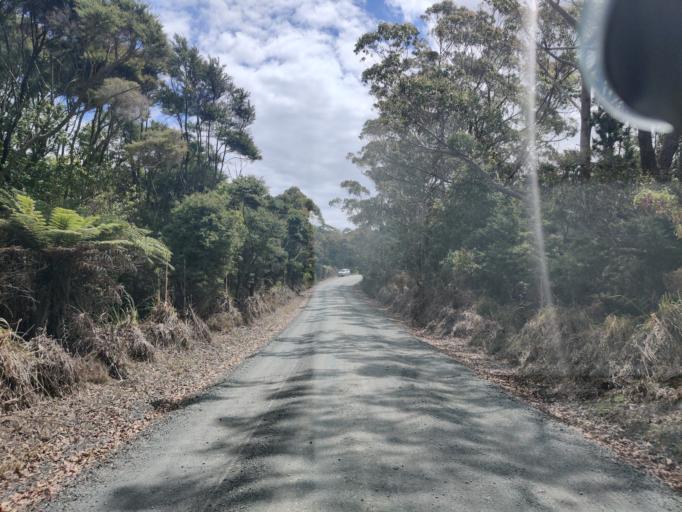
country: NZ
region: Northland
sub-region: Far North District
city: Paihia
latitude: -35.2597
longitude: 174.0549
